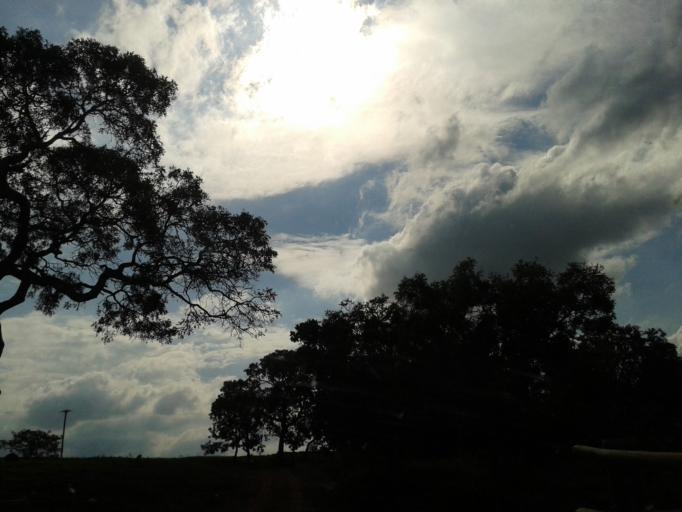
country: BR
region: Minas Gerais
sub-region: Campina Verde
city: Campina Verde
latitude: -19.3904
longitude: -49.6981
